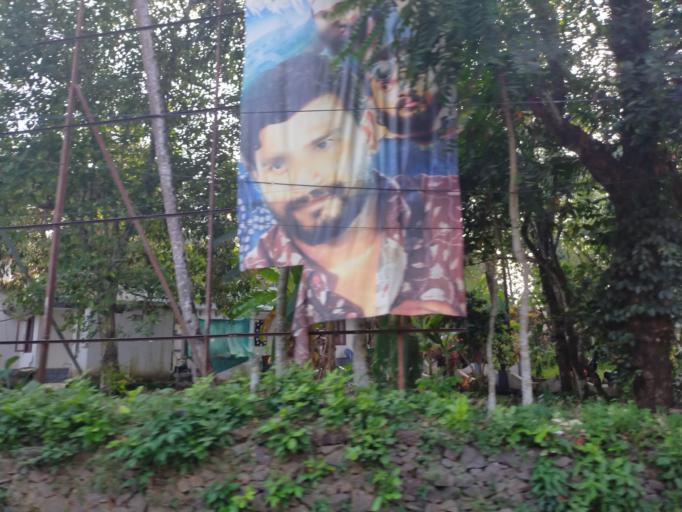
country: IN
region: Kerala
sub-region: Kottayam
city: Palackattumala
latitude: 9.7410
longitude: 76.5158
